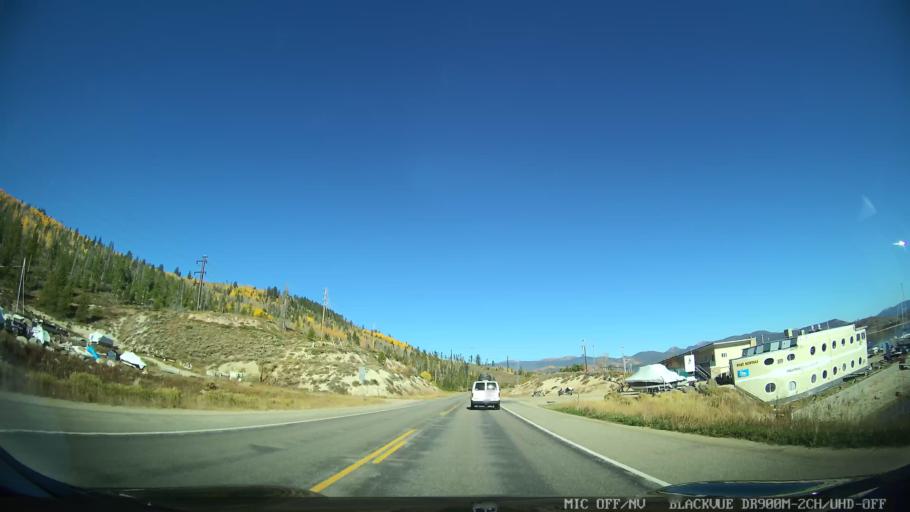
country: US
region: Colorado
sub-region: Grand County
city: Granby
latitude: 40.1599
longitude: -105.8935
